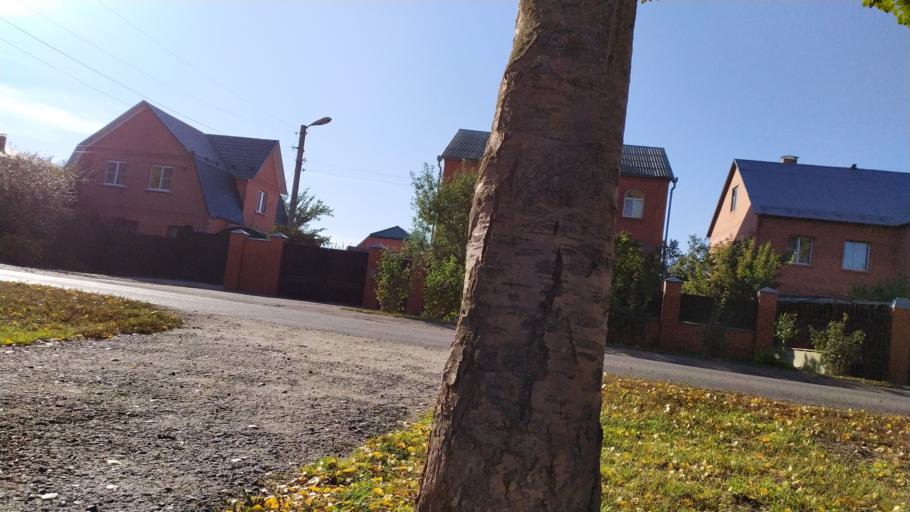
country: RU
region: Kursk
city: Kursk
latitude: 51.6433
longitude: 36.1395
